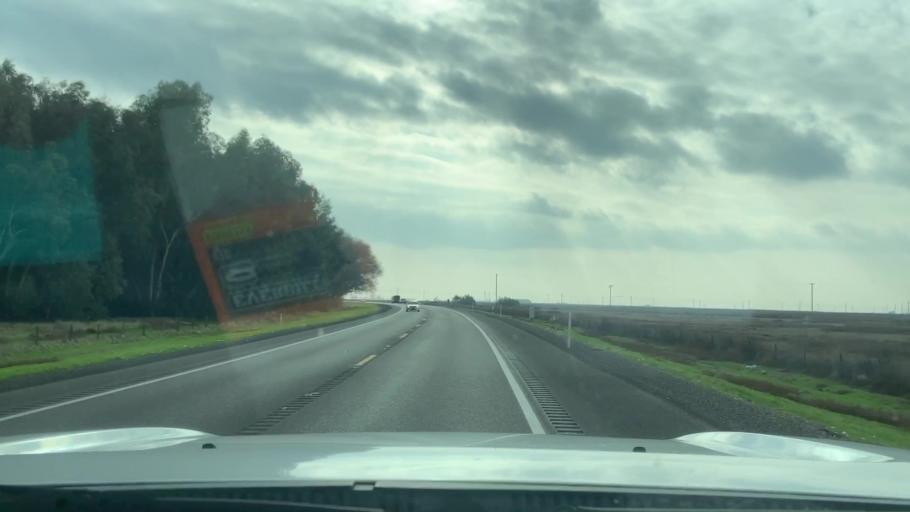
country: US
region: California
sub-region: Kings County
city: Stratford
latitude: 36.2486
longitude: -119.8139
